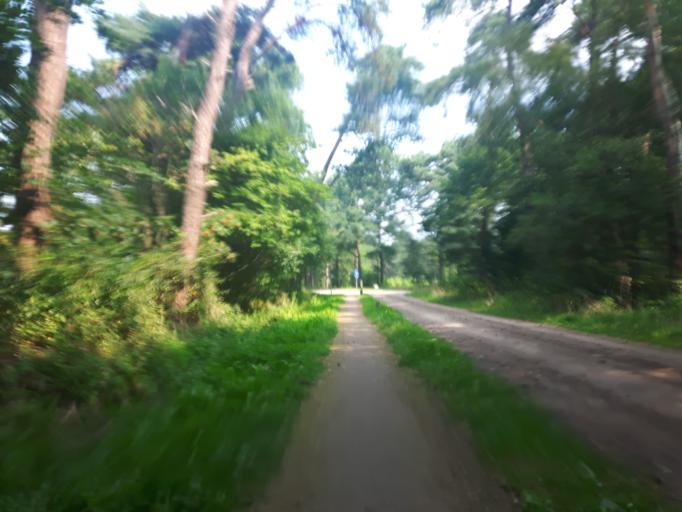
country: NL
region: Overijssel
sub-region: Gemeente Hof van Twente
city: Delden
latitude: 52.2977
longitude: 6.7030
